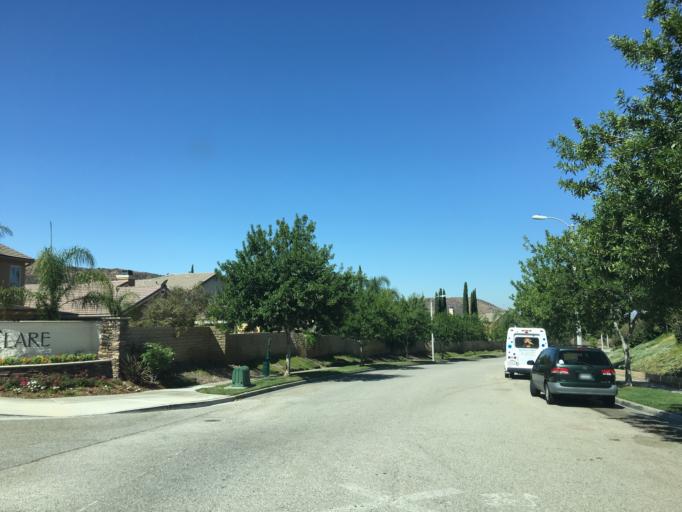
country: US
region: California
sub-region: Los Angeles County
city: Santa Clarita
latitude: 34.4434
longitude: -118.4760
